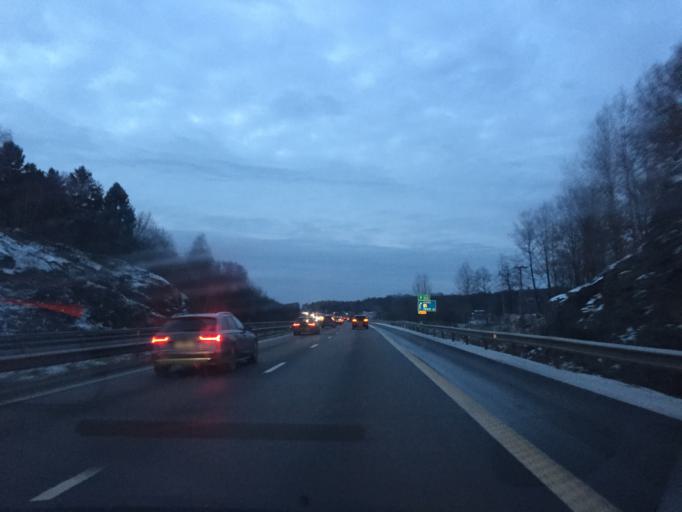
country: SE
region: Vaestra Goetaland
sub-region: Kungalvs Kommun
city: Kode
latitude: 57.9320
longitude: 11.8725
